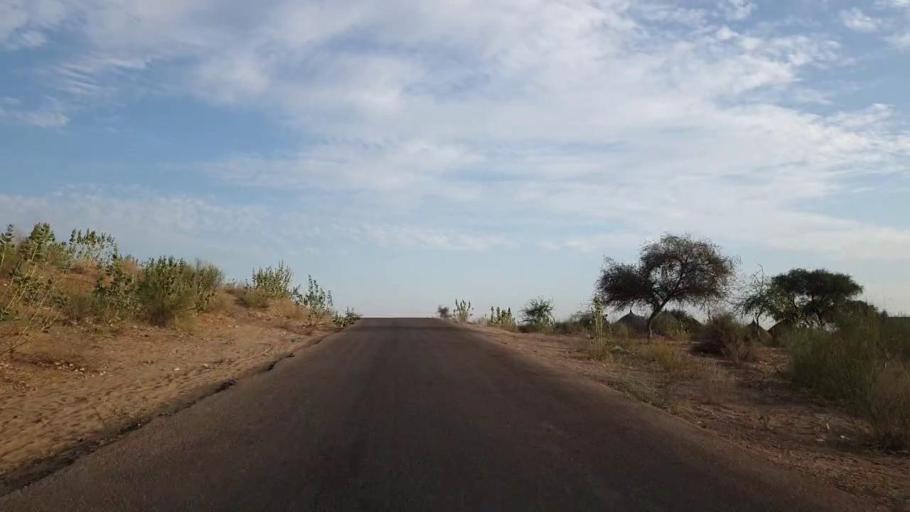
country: PK
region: Sindh
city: Umarkot
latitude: 25.1616
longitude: 70.0064
